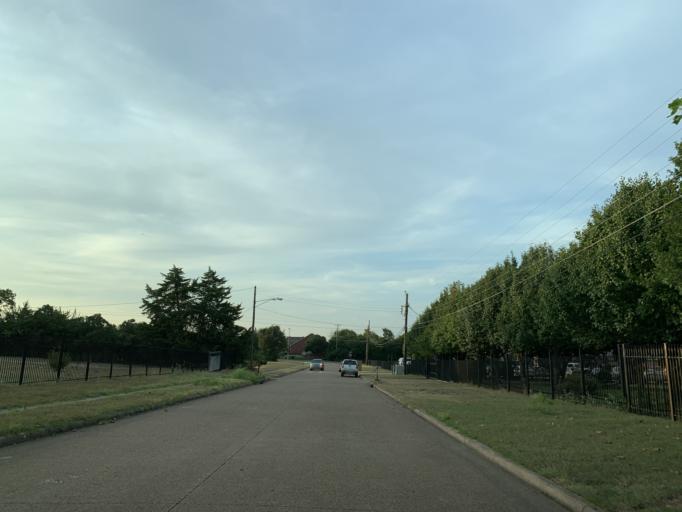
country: US
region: Texas
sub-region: Dallas County
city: Cockrell Hill
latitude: 32.7044
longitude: -96.8871
